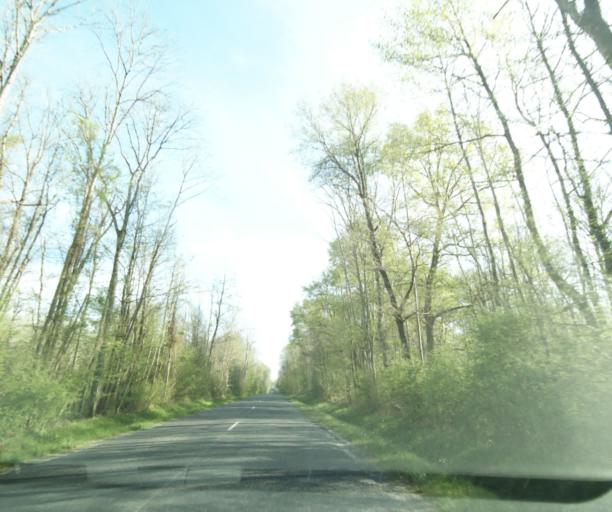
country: FR
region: Ile-de-France
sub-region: Departement de Seine-et-Marne
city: Nangis
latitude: 48.5263
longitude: 2.9760
